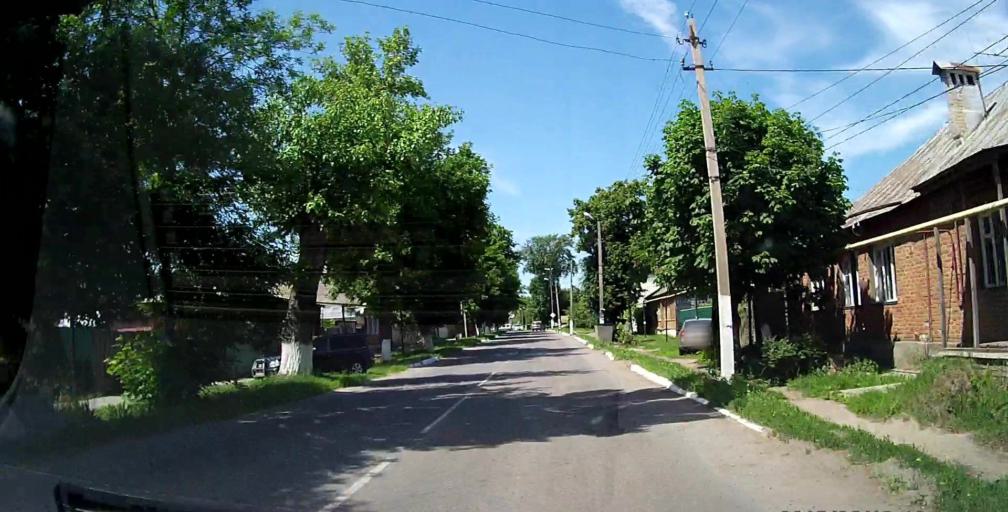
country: RU
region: Lipetsk
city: Chaplygin
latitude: 53.2432
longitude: 39.9718
